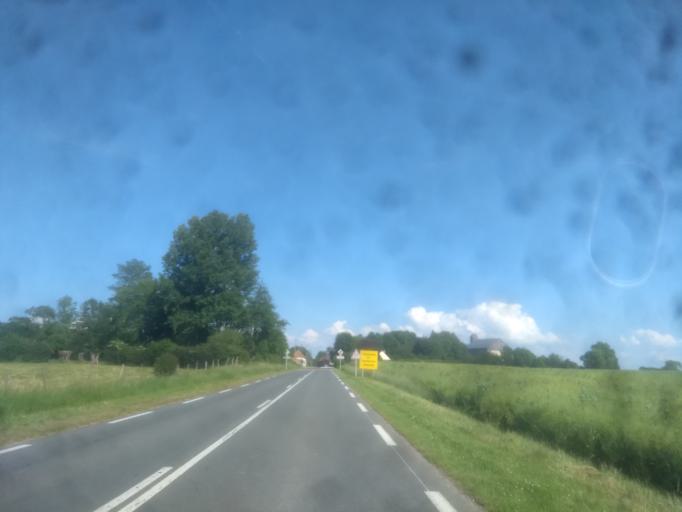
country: FR
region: Picardie
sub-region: Departement de la Somme
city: Bernaville
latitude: 50.1421
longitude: 2.1126
